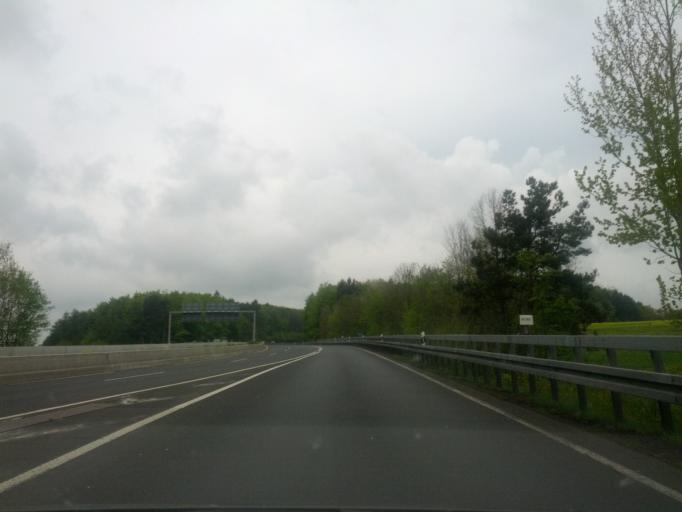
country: DE
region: Hesse
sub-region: Regierungsbezirk Giessen
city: Reiskirchen
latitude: 50.6106
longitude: 8.8209
